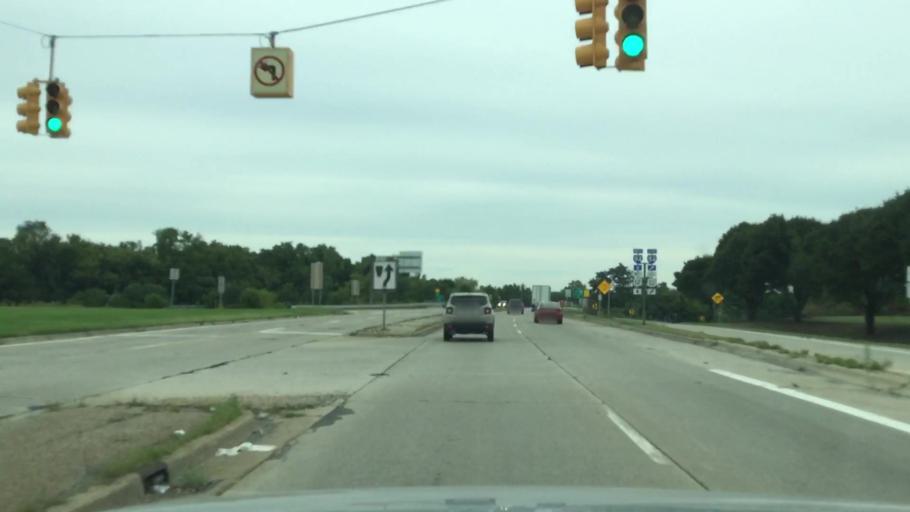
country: US
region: Michigan
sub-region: Washtenaw County
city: Ypsilanti
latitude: 42.2270
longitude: -83.6174
